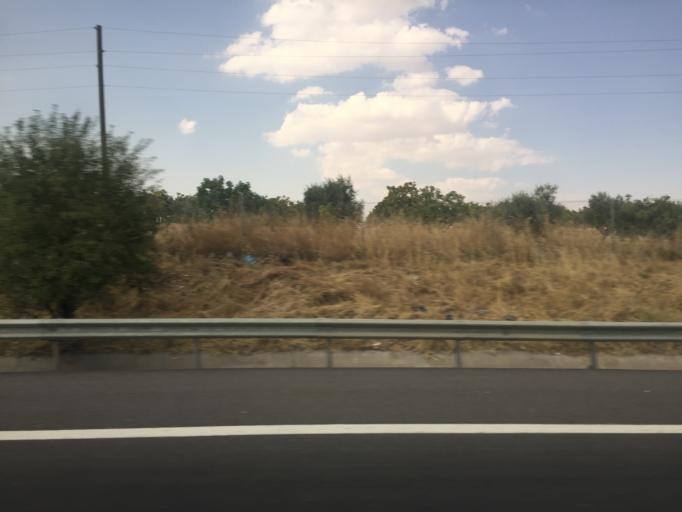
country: TR
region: Sanliurfa
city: Akziyaret
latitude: 37.2711
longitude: 38.8005
